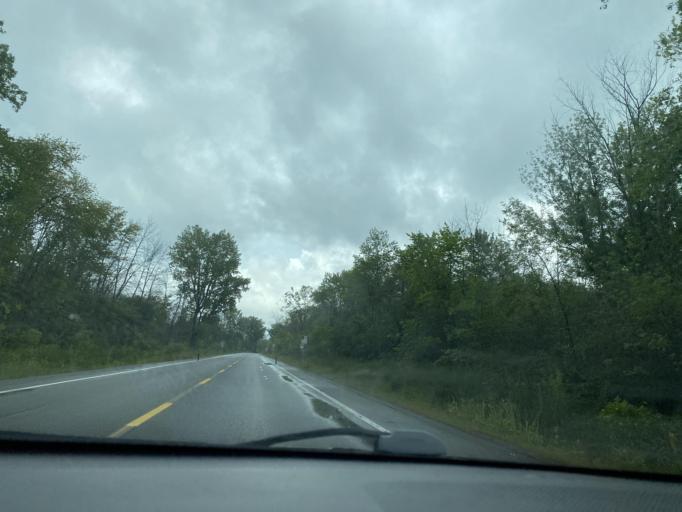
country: CA
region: Quebec
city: Baie-D'Urfe
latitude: 45.4486
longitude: -73.9280
